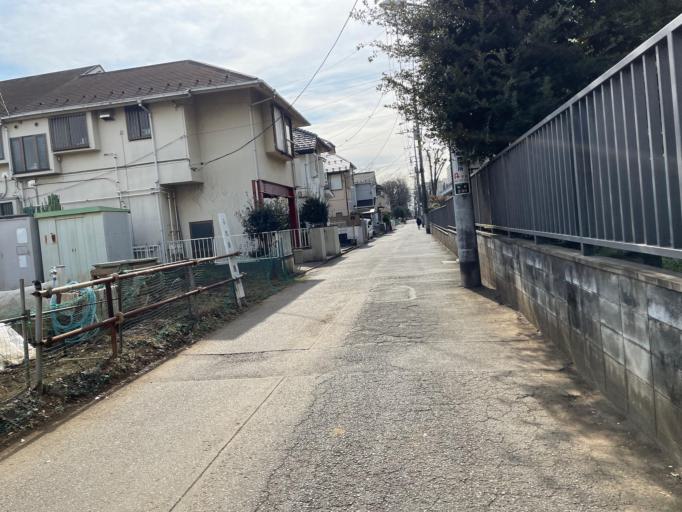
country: JP
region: Tokyo
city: Nishi-Tokyo-shi
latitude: 35.7003
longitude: 139.5209
